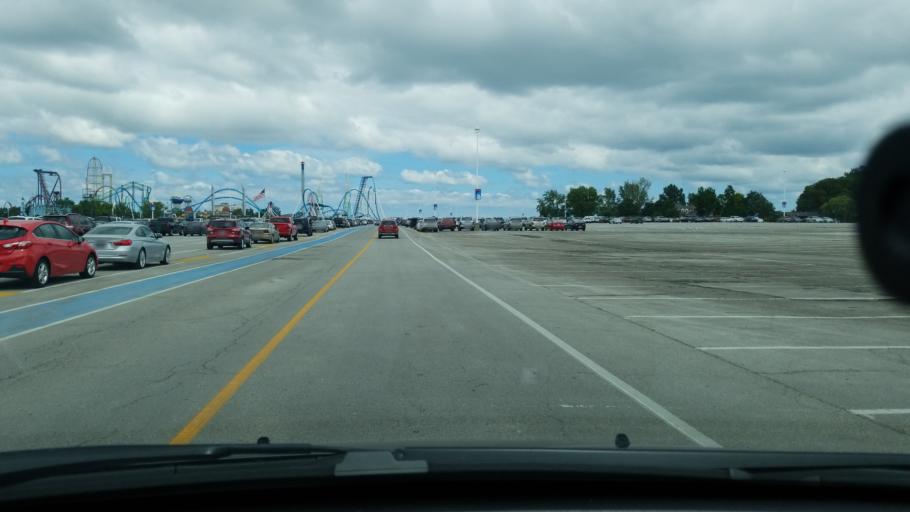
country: US
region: Ohio
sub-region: Erie County
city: Sandusky
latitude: 41.4736
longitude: -82.6759
